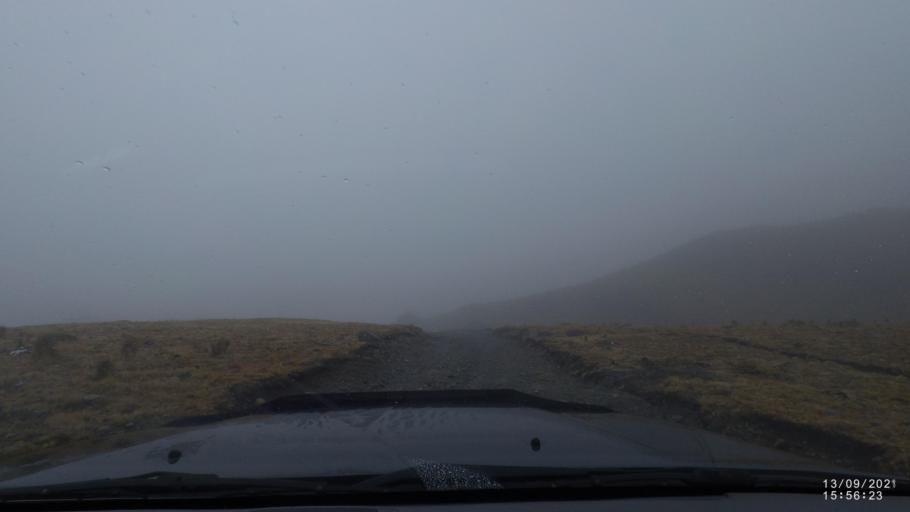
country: BO
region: Cochabamba
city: Colomi
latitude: -17.3039
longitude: -65.7072
